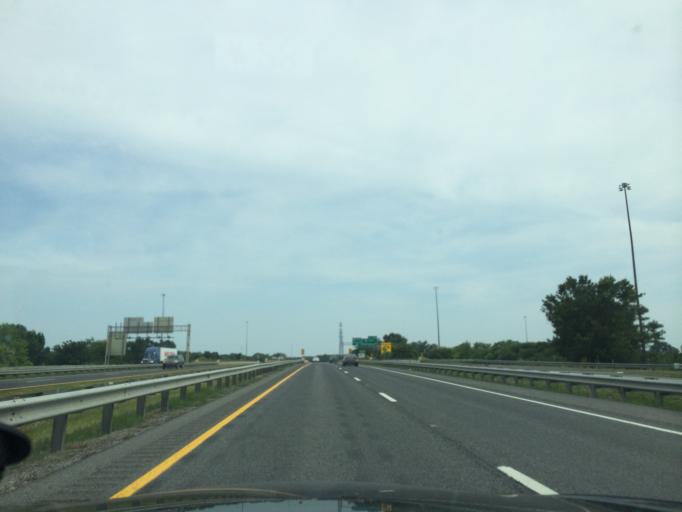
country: US
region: Maryland
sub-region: Washington County
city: Halfway
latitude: 39.6185
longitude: -77.7868
